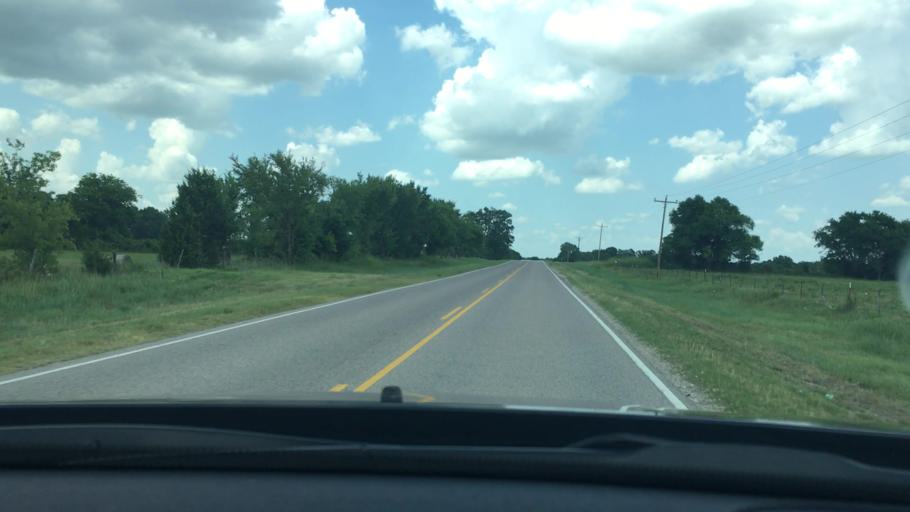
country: US
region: Oklahoma
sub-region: Johnston County
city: Tishomingo
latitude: 34.4764
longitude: -96.6323
